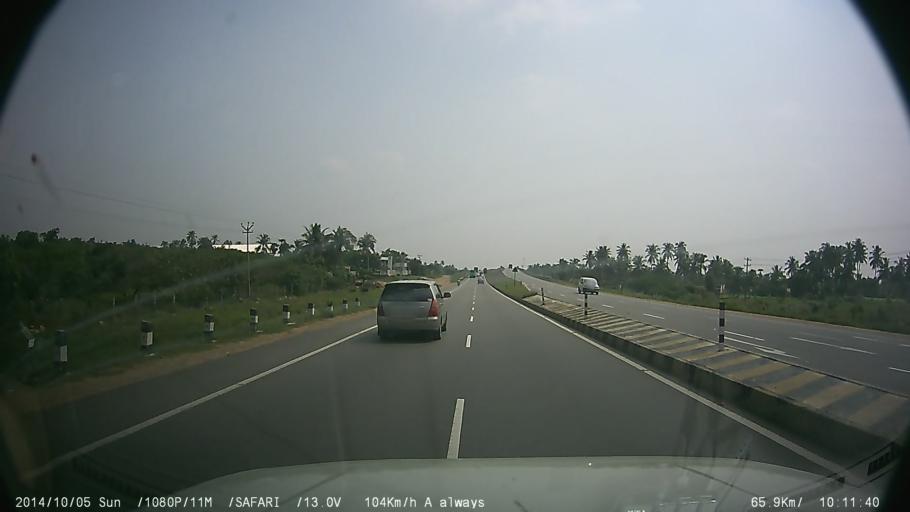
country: IN
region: Tamil Nadu
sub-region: Salem
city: Ilampillai
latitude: 11.5418
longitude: 77.9760
